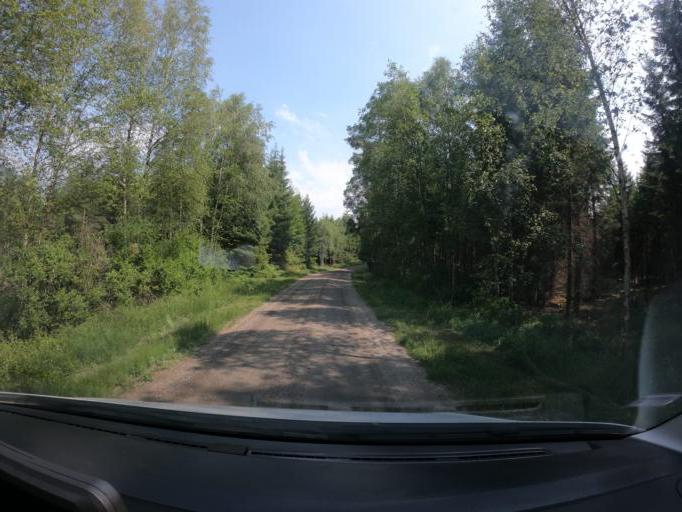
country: SE
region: Kronoberg
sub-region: Markaryds Kommun
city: Markaryd
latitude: 56.3820
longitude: 13.5520
